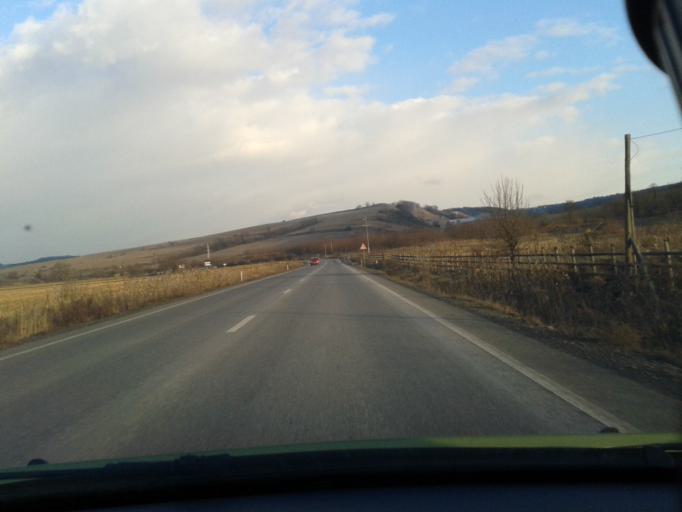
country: RO
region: Sibiu
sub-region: Comuna Copsa Mica
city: Copsa Mica
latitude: 46.1192
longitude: 24.2717
